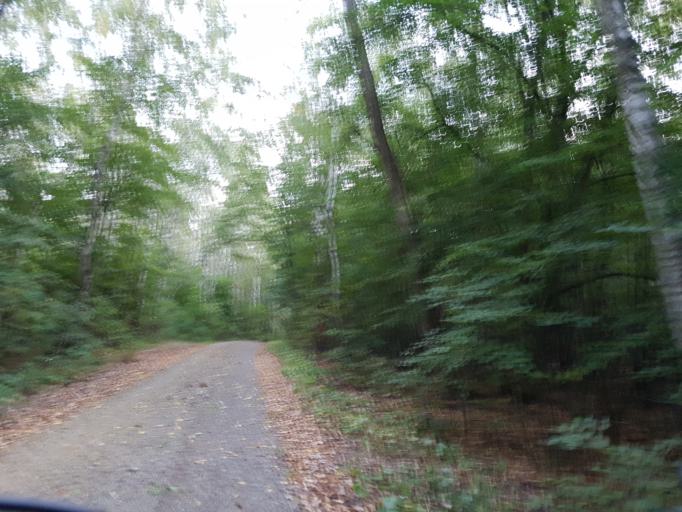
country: DE
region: Brandenburg
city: Trobitz
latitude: 51.5751
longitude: 13.4464
